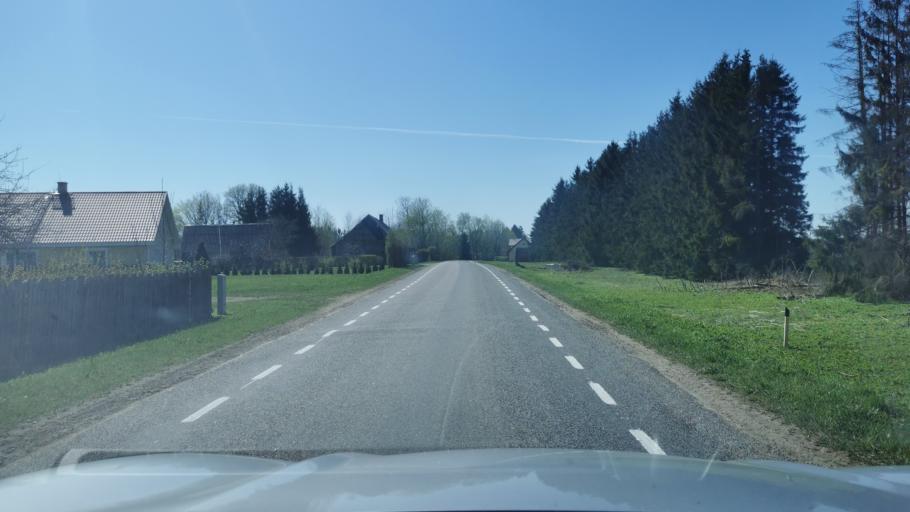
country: EE
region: Laeaene-Virumaa
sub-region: Vinni vald
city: Vinni
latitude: 59.0972
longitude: 26.6166
